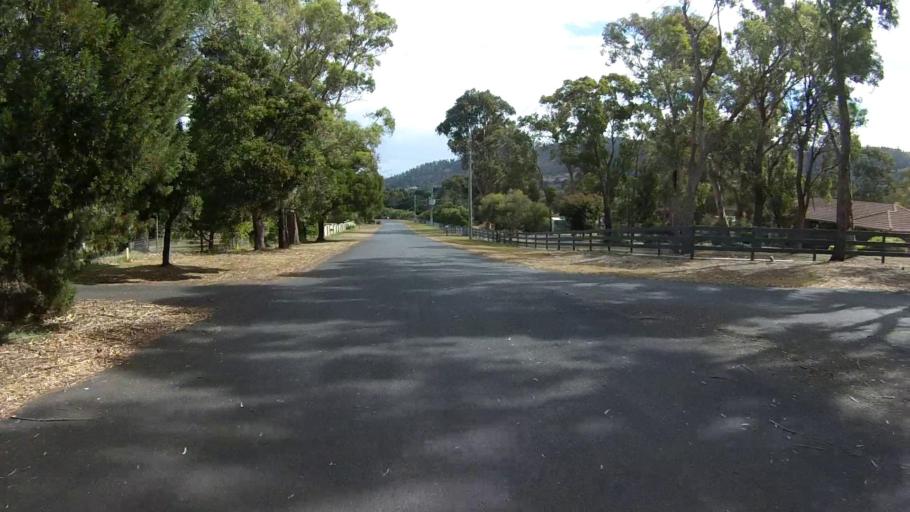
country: AU
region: Tasmania
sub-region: Clarence
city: Acton Park
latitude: -42.8808
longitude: 147.4925
